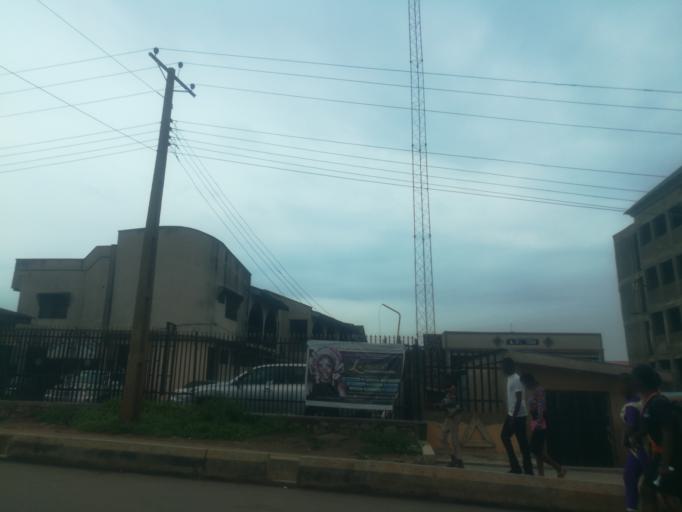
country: NG
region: Oyo
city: Ibadan
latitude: 7.3960
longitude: 3.9234
